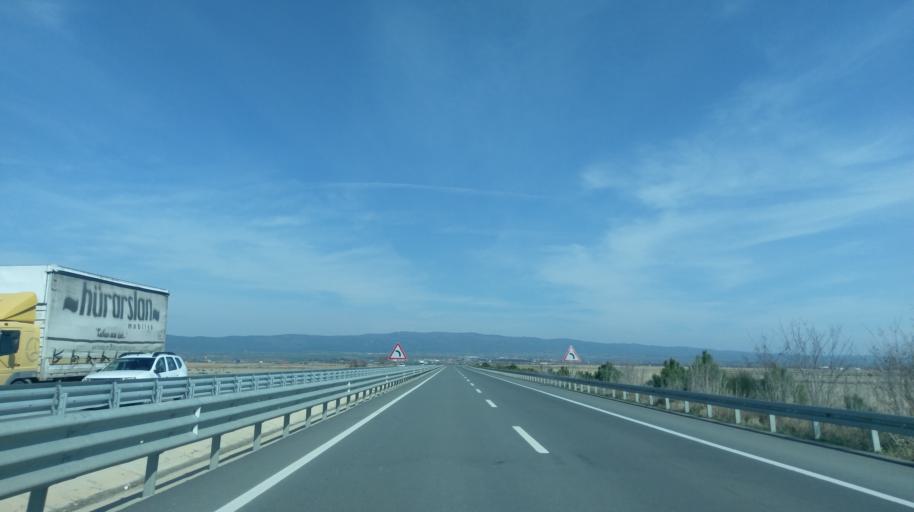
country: TR
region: Canakkale
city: Evrese
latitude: 40.6256
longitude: 26.8687
